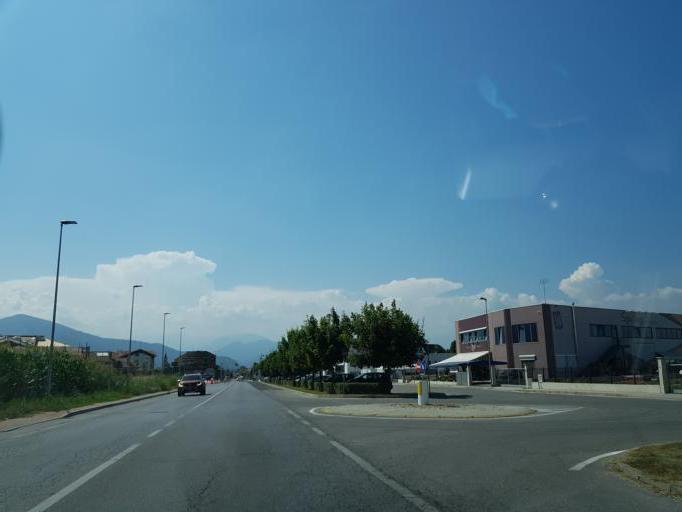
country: IT
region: Piedmont
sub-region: Provincia di Cuneo
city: San Rocco
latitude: 44.3970
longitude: 7.4810
